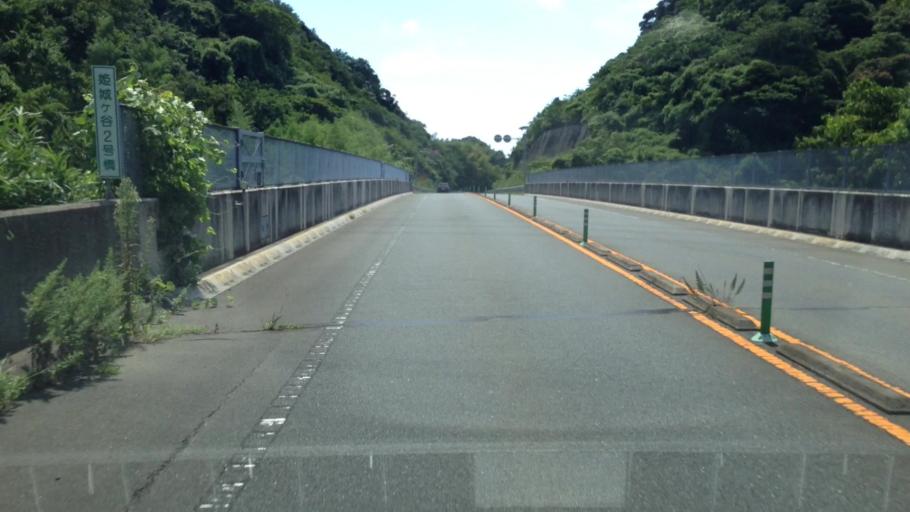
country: JP
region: Kanagawa
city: Yokosuka
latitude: 35.2356
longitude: 139.6510
